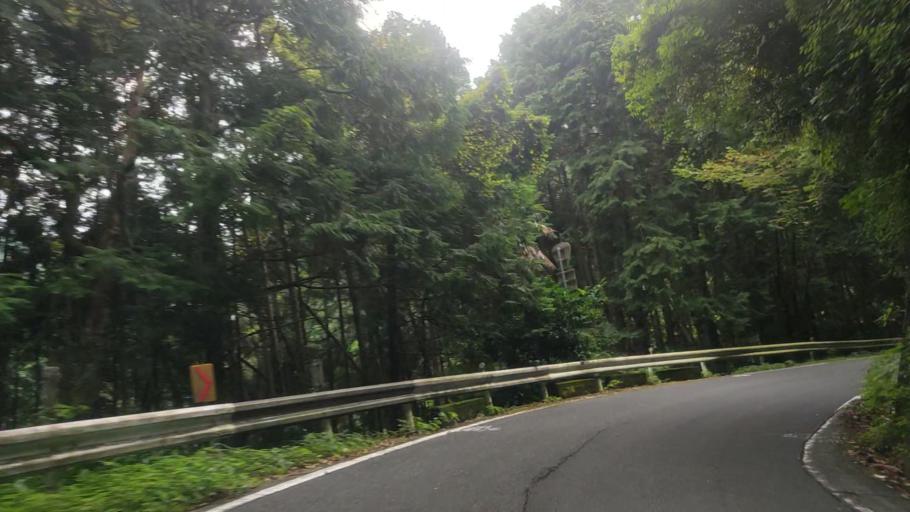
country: JP
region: Wakayama
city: Koya
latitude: 34.2496
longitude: 135.5453
